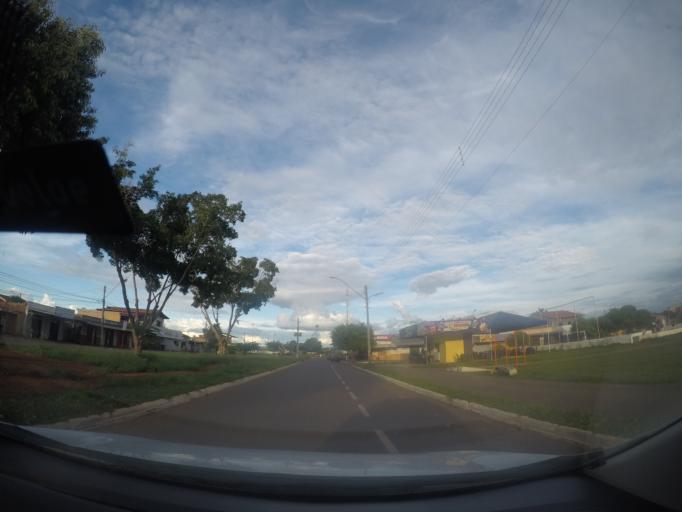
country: BR
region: Goias
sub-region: Goianira
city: Goianira
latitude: -16.5898
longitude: -49.3779
